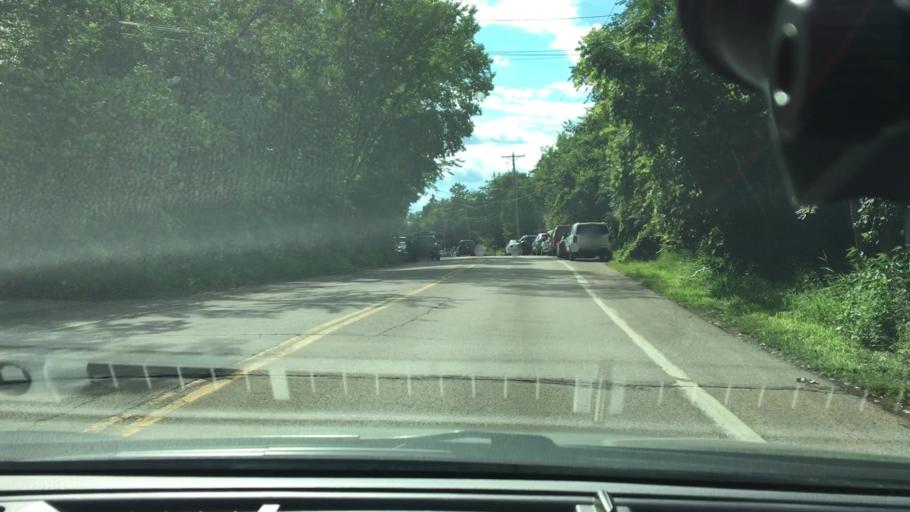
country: US
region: Minnesota
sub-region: Hennepin County
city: Mound
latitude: 44.9307
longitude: -93.6663
